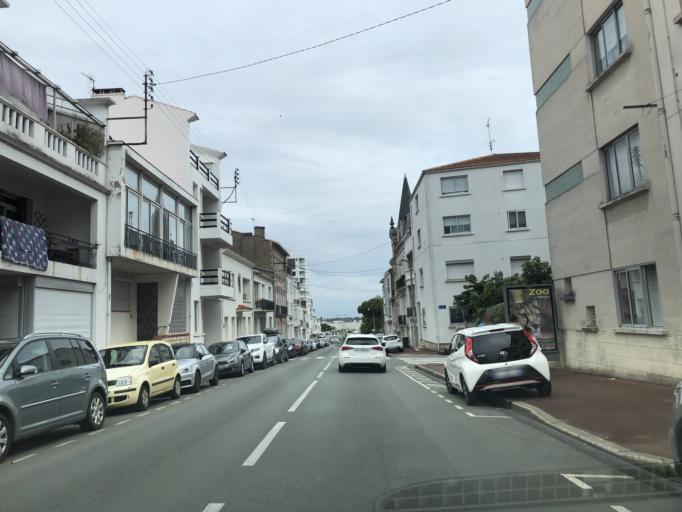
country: FR
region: Poitou-Charentes
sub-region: Departement de la Charente-Maritime
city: Royan
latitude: 45.6210
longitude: -1.0371
